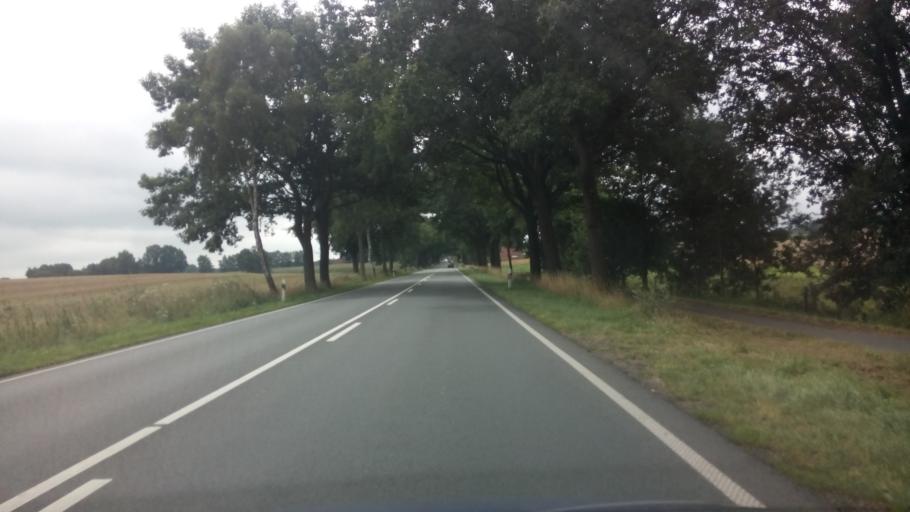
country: DE
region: Lower Saxony
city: Bassum
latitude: 52.8806
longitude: 8.7288
